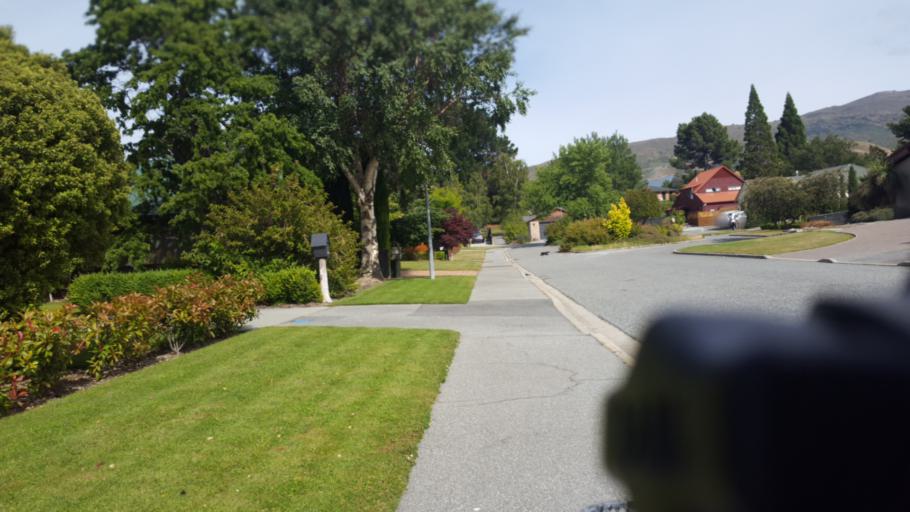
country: NZ
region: Otago
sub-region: Queenstown-Lakes District
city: Wanaka
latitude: -45.0447
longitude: 169.1927
